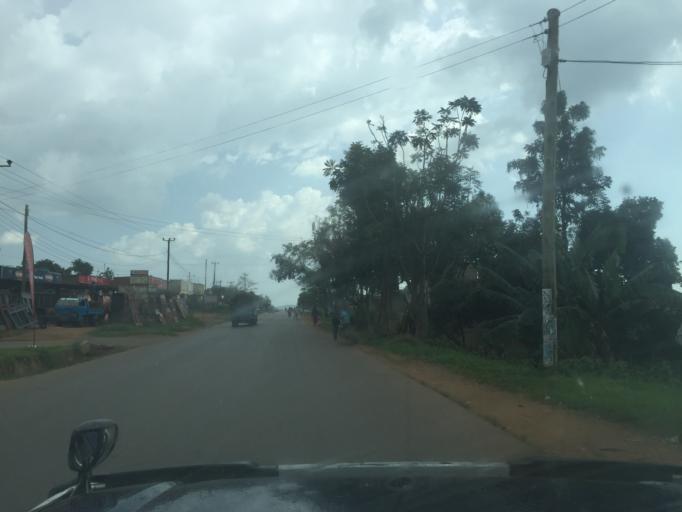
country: UG
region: Central Region
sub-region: Luwero District
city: Wobulenzi
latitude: 0.5891
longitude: 32.5323
